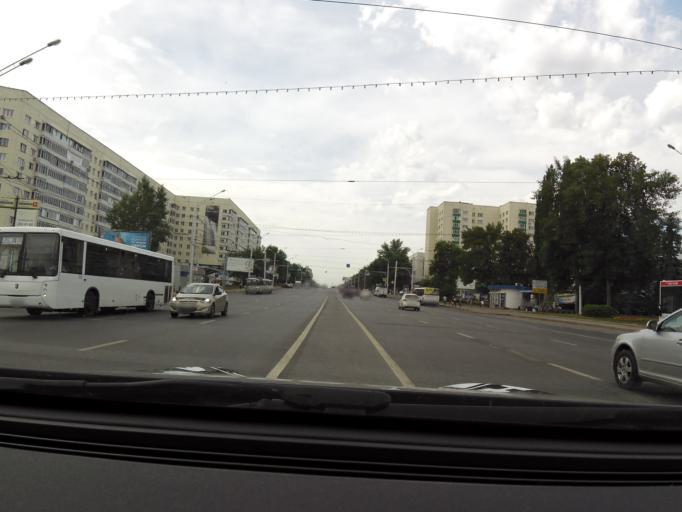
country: RU
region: Bashkortostan
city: Ufa
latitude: 54.7958
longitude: 56.0387
